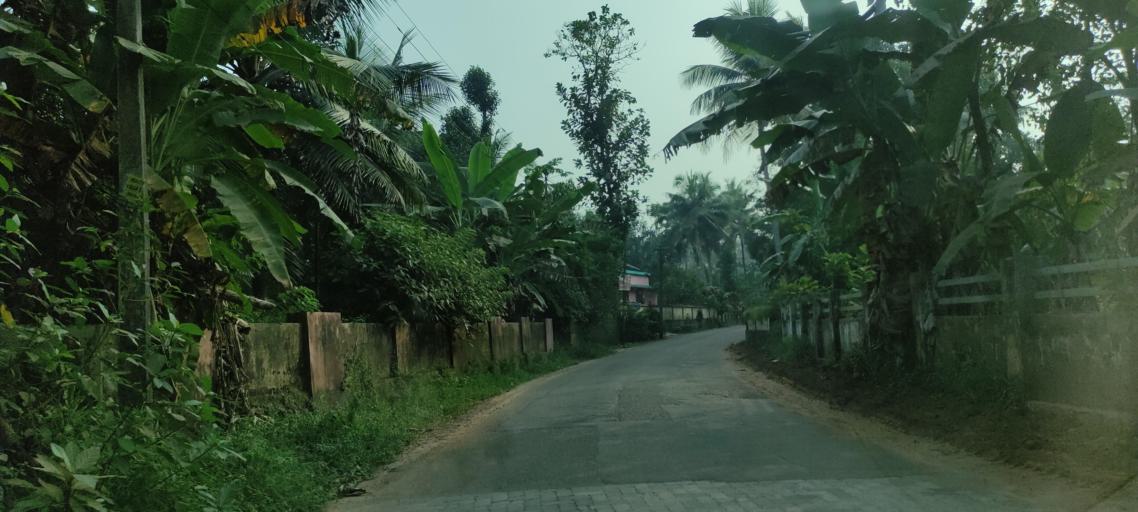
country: IN
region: Kerala
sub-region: Ernakulam
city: Piravam
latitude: 9.7884
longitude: 76.4985
